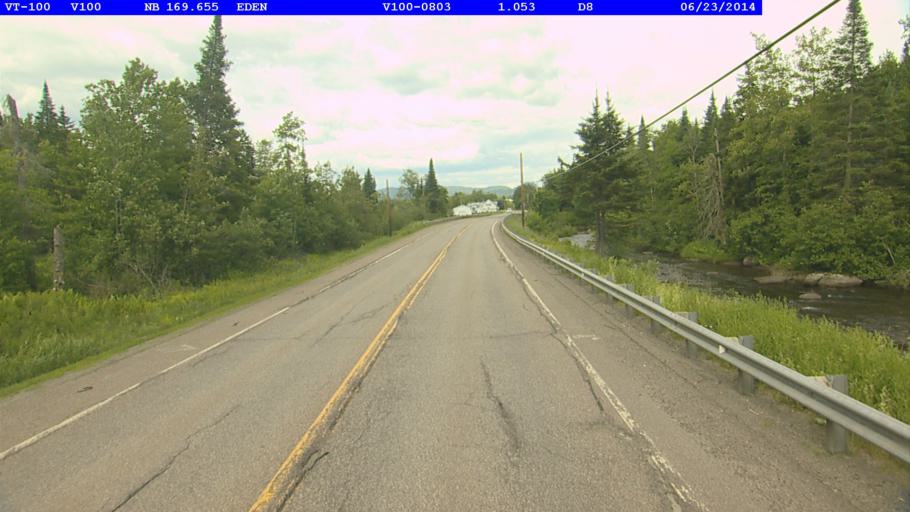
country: US
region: Vermont
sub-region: Lamoille County
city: Hyde Park
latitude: 44.6959
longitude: -72.5788
